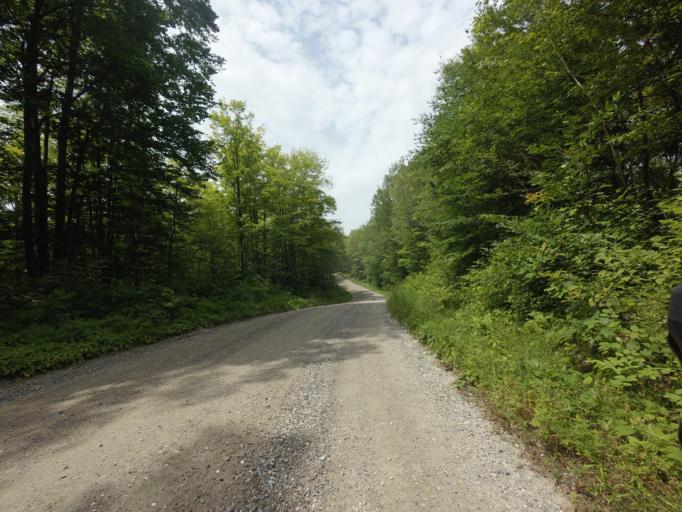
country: CA
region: Ontario
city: Perth
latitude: 44.7813
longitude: -76.6196
